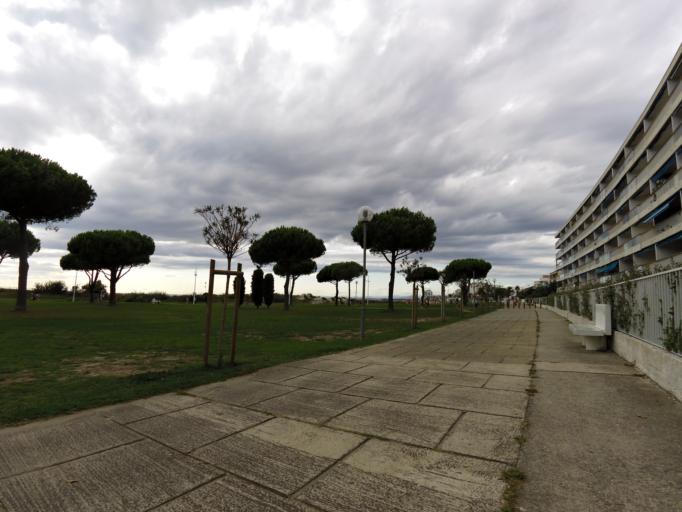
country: FR
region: Languedoc-Roussillon
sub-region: Departement du Gard
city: Le Grau-du-Roi
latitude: 43.5303
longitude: 4.1410
